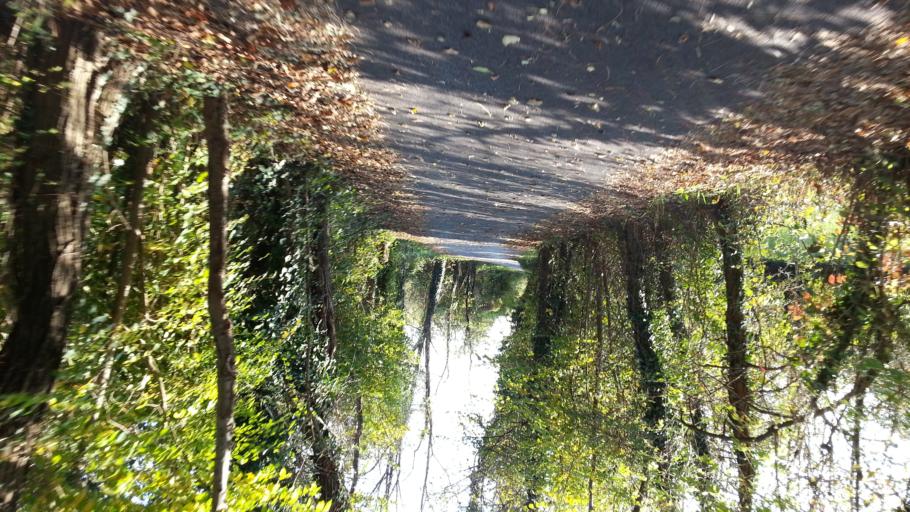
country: IT
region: Friuli Venezia Giulia
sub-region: Provincia di Udine
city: Venzone
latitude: 46.3239
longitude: 13.1283
